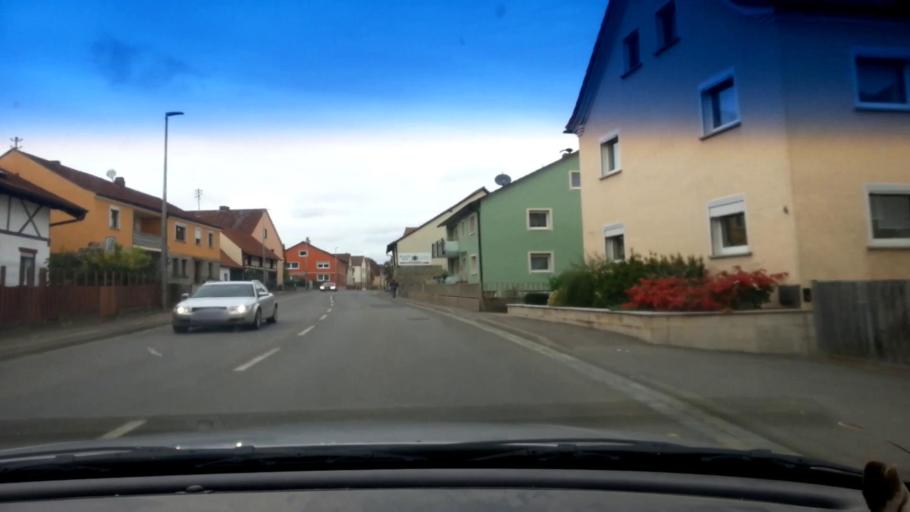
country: DE
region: Bavaria
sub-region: Upper Franconia
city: Reckendorf
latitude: 50.0169
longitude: 10.8275
